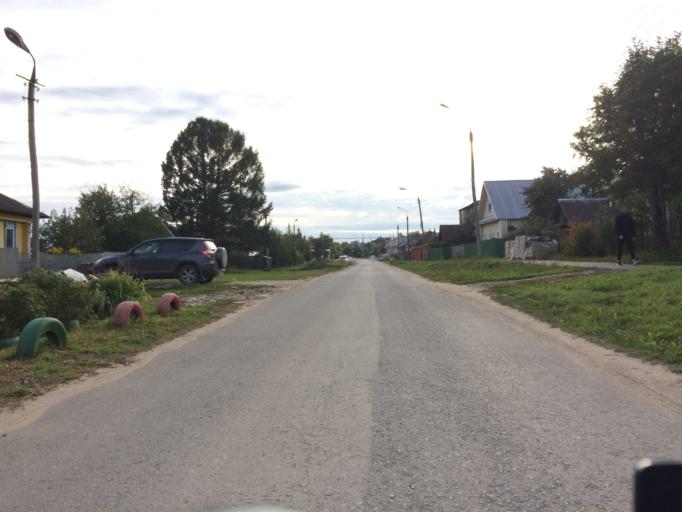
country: RU
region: Mariy-El
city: Yoshkar-Ola
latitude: 56.6516
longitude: 47.9832
